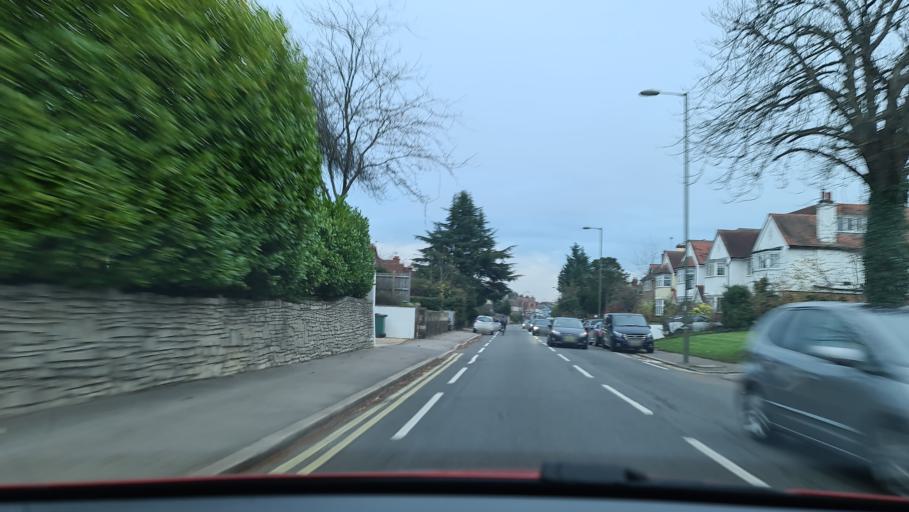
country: GB
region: England
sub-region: Surrey
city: Thames Ditton
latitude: 51.3875
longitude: -0.3289
